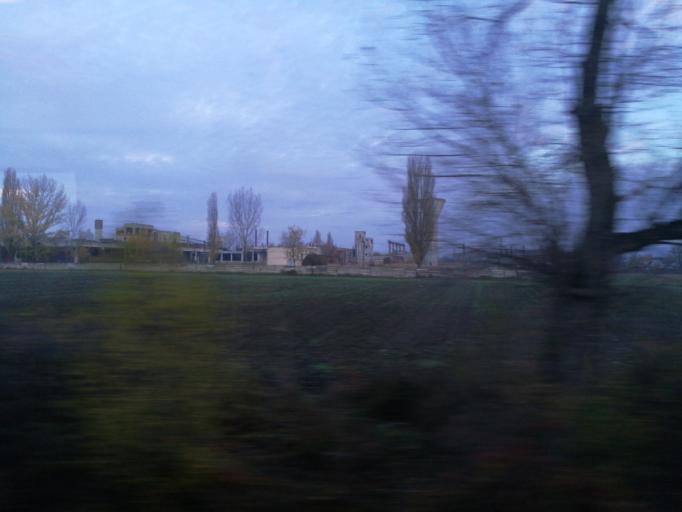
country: RO
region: Prahova
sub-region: Comuna Berceni
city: Berceni
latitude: 44.9422
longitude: 26.1076
